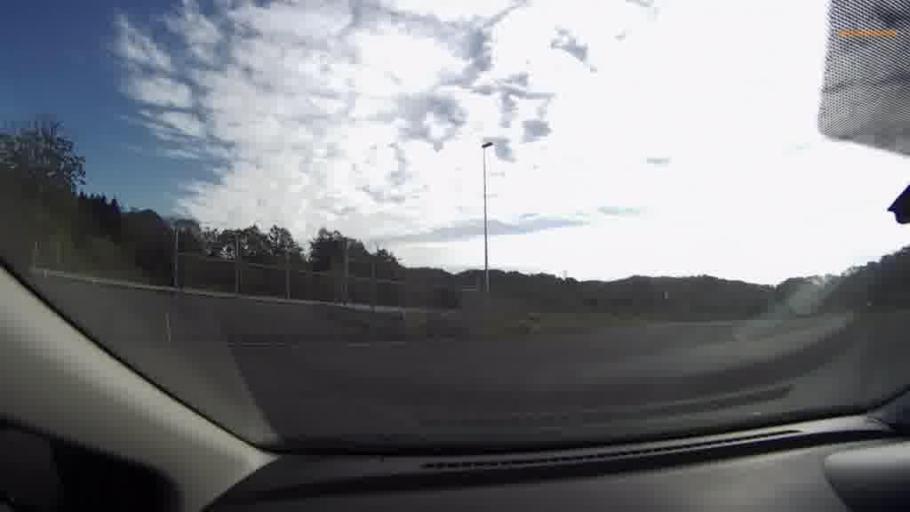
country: JP
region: Hokkaido
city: Kushiro
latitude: 43.0775
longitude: 143.9627
